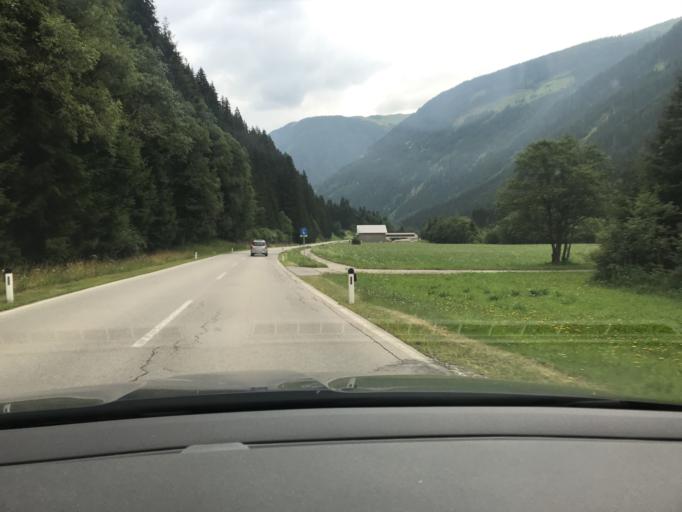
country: AT
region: Tyrol
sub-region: Politischer Bezirk Lienz
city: Hopfgarten in Defereggen
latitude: 46.9258
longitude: 12.4689
